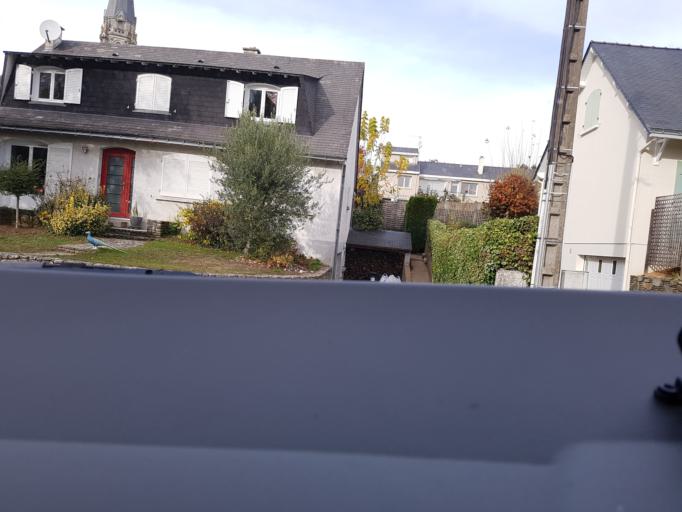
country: FR
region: Pays de la Loire
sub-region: Departement de Maine-et-Loire
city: Beaupreau
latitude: 47.2012
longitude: -0.9901
